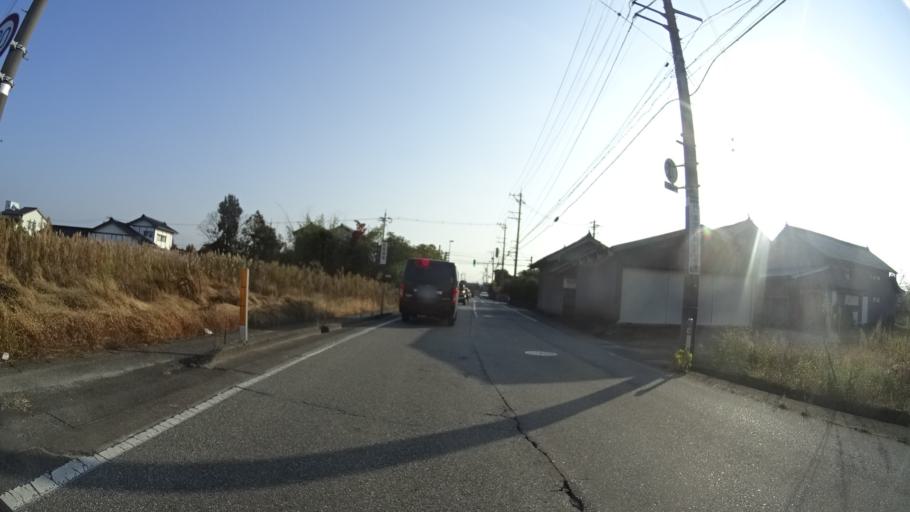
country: JP
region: Toyama
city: Toyama-shi
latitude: 36.6892
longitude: 137.2711
